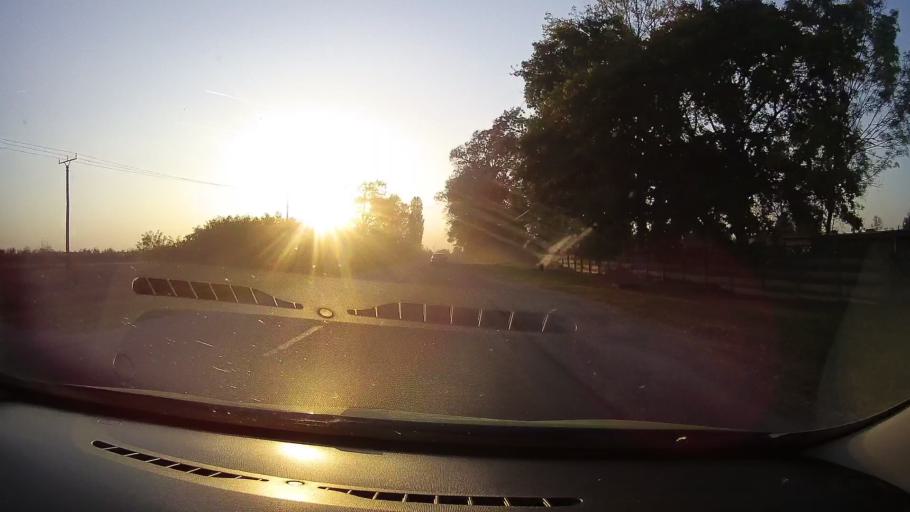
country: RO
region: Arad
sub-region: Comuna Ineu
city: Ineu
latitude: 46.4299
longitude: 21.8263
